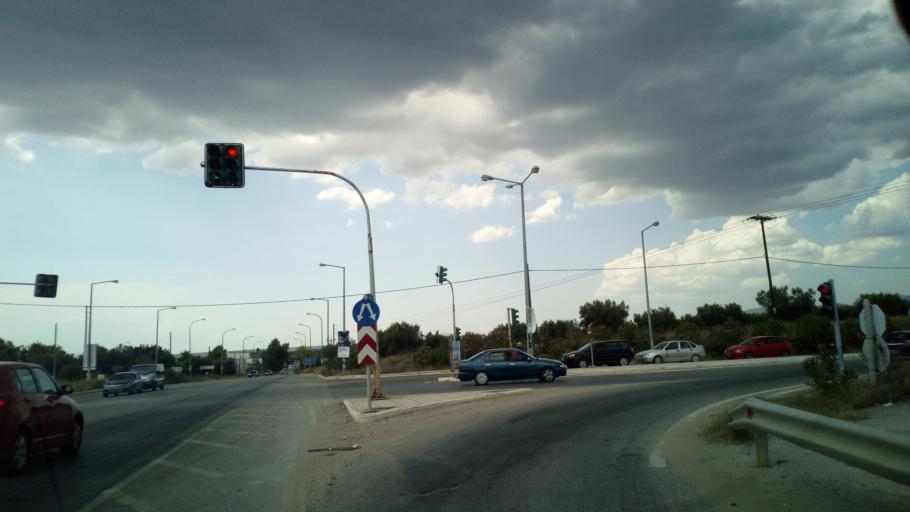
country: GR
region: Central Macedonia
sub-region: Nomos Chalkidikis
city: Kalyves Polygyrou
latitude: 40.2795
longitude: 23.4303
